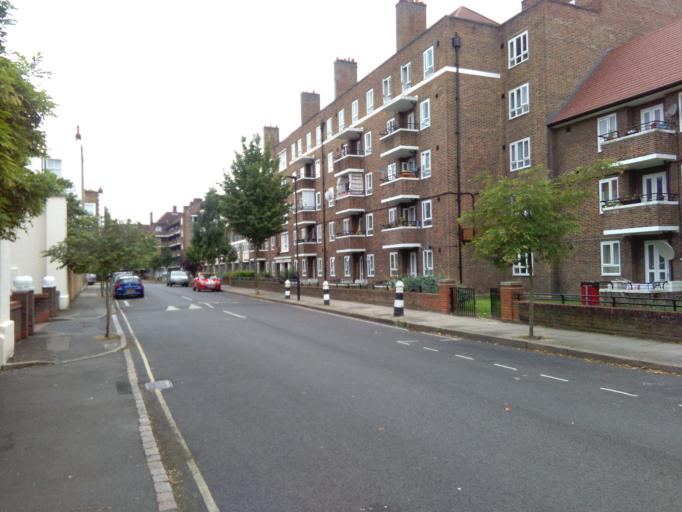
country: GB
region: England
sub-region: Greater London
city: Kennington
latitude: 51.4806
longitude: -0.1183
